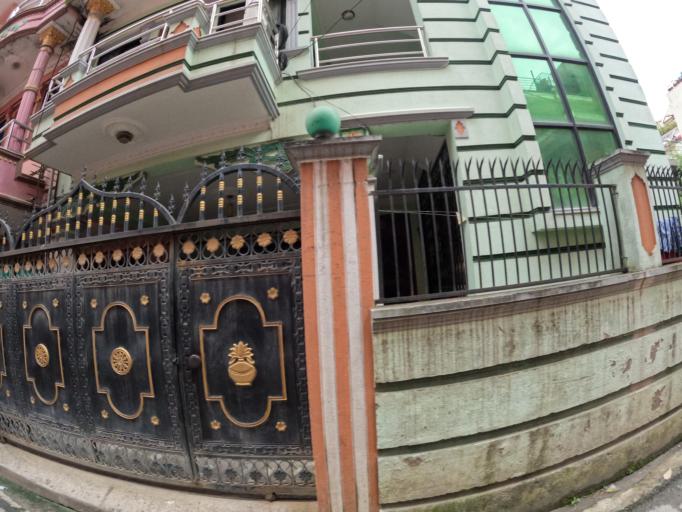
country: NP
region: Central Region
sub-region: Bagmati Zone
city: Kathmandu
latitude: 27.7432
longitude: 85.3161
